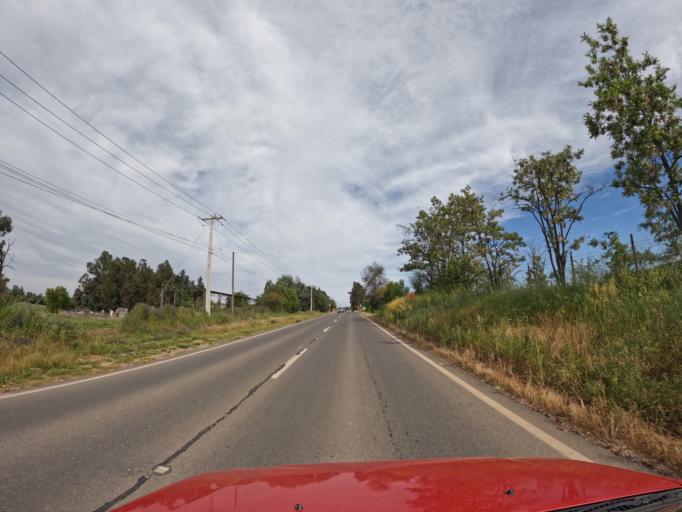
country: CL
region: Maule
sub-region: Provincia de Talca
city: Talca
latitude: -35.3885
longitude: -71.8158
